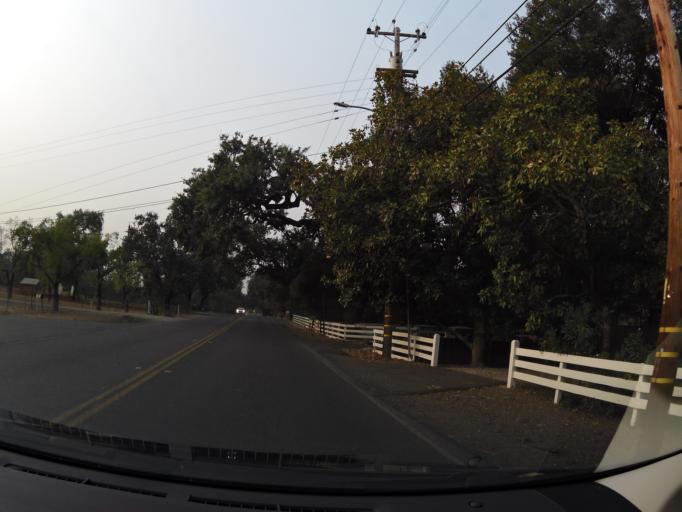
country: US
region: California
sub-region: Sonoma County
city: Fetters Hot Springs-Agua Caliente
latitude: 38.3176
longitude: -122.5007
